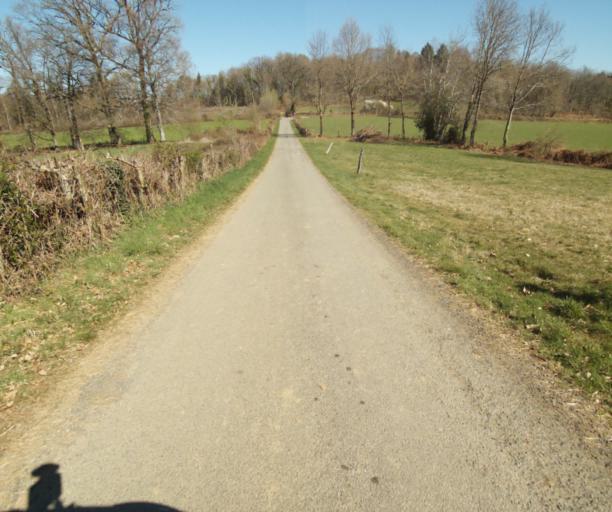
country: FR
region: Limousin
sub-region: Departement de la Correze
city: Saint-Clement
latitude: 45.3366
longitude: 1.6545
